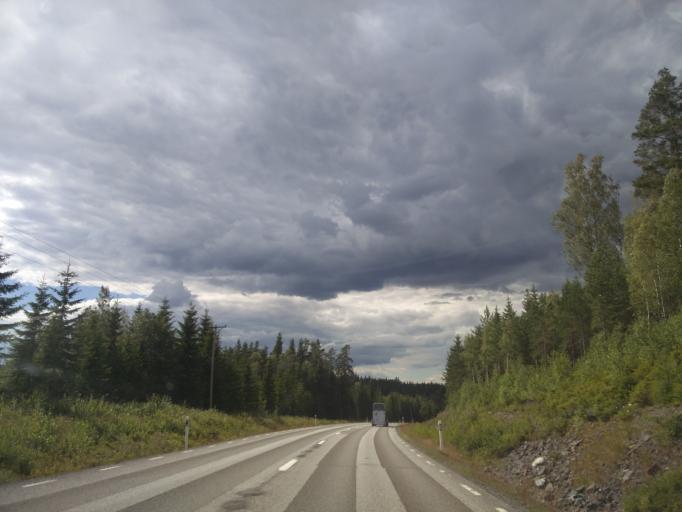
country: SE
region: OErebro
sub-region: Hallefors Kommun
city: Haellefors
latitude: 59.7657
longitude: 14.4113
